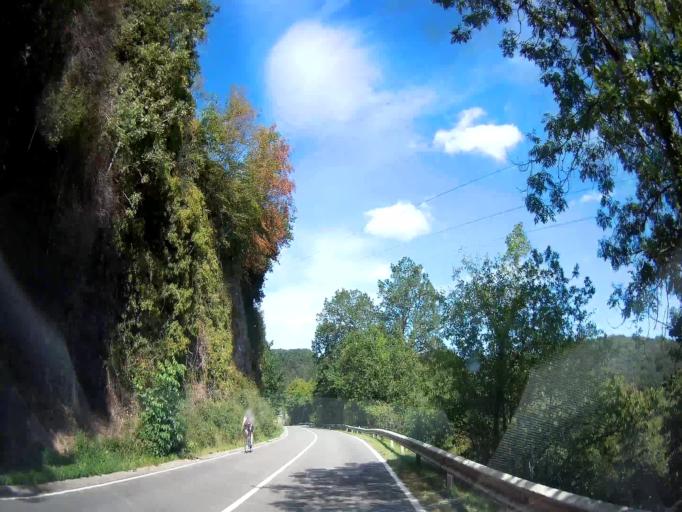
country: BE
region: Wallonia
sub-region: Province du Luxembourg
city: Rendeux
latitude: 50.2059
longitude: 5.5366
